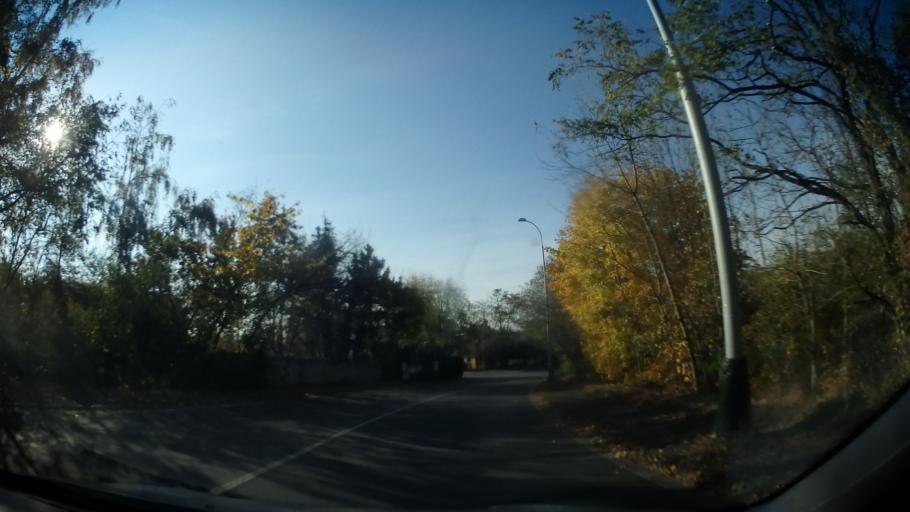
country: CZ
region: Central Bohemia
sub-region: Okres Praha-Vychod
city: Ricany
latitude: 50.0005
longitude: 14.6640
